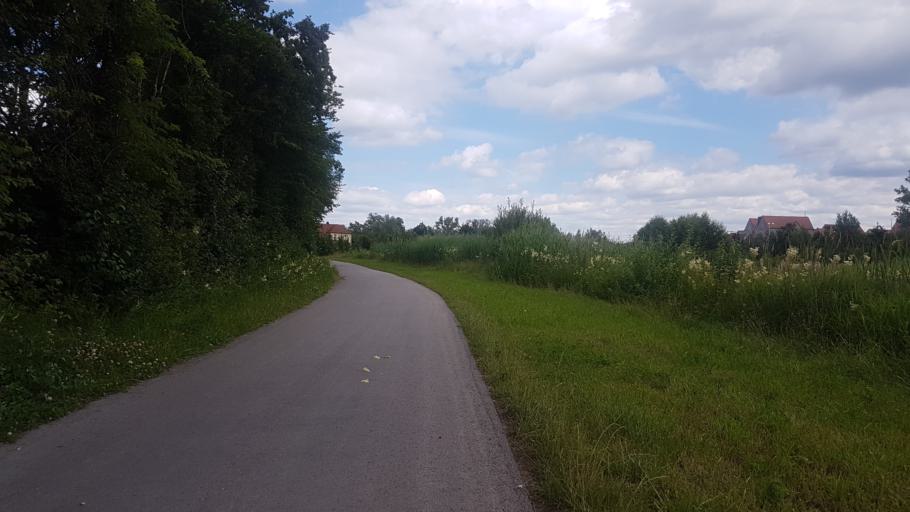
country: DE
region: Bavaria
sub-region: Regierungsbezirk Mittelfranken
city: Gunzenhausen
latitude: 49.1124
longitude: 10.7507
